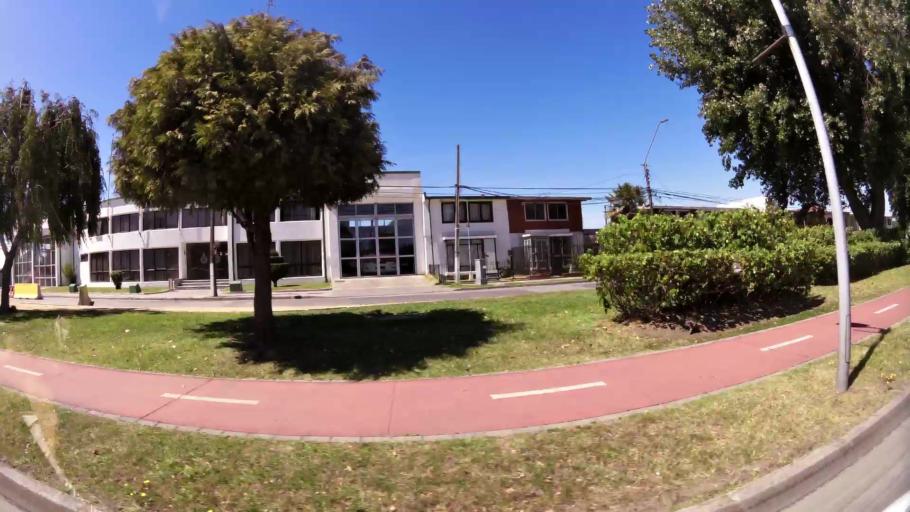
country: CL
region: Biobio
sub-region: Provincia de Concepcion
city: Talcahuano
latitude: -36.7550
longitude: -73.0920
